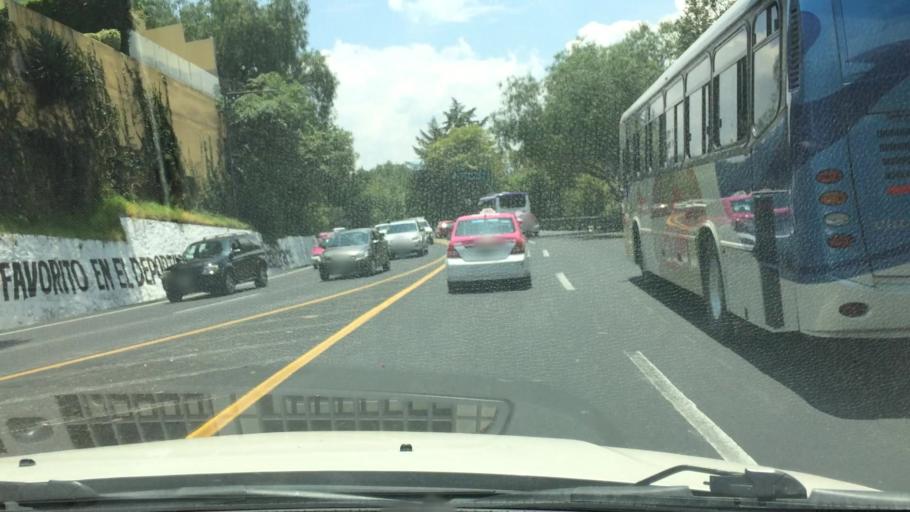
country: MX
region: Mexico City
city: Tlalpan
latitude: 19.2726
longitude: -99.1679
